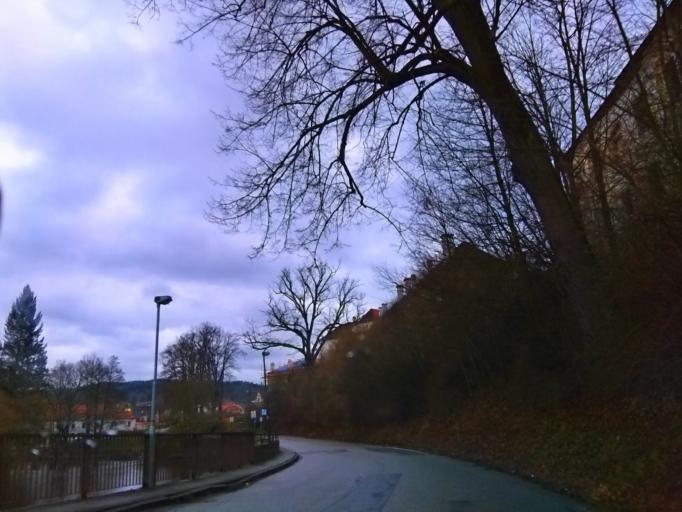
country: CZ
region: Jihocesky
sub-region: Okres Cesky Krumlov
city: Vyssi Brod
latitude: 48.6220
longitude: 14.3071
